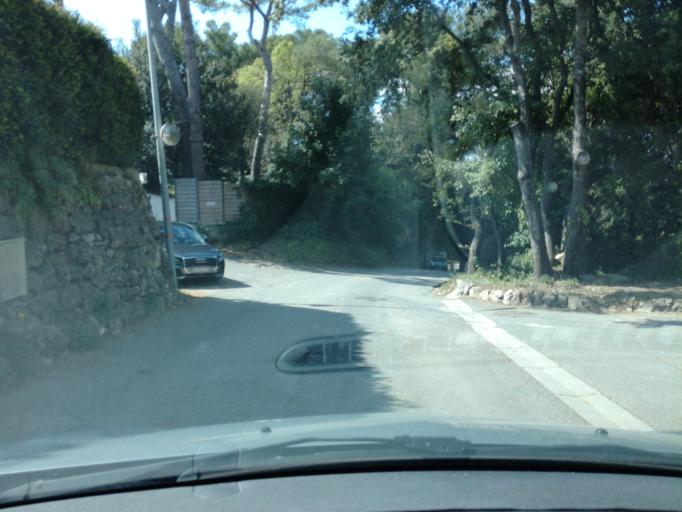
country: FR
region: Provence-Alpes-Cote d'Azur
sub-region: Departement des Alpes-Maritimes
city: Mougins
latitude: 43.6080
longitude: 6.9913
